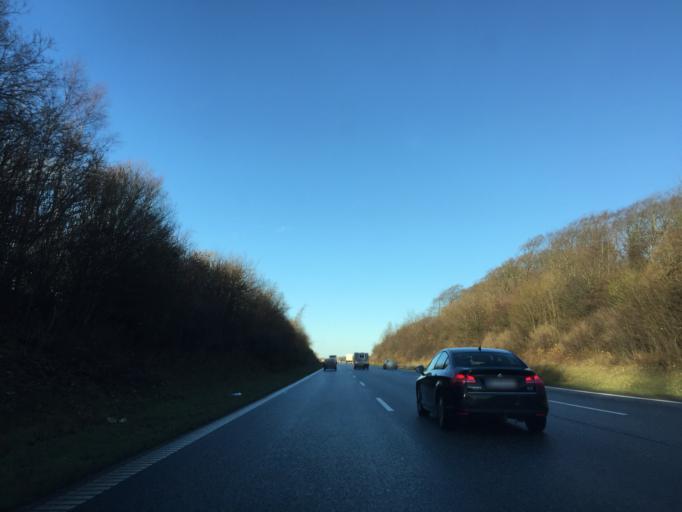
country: DK
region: South Denmark
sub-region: Fredericia Kommune
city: Taulov
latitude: 55.6056
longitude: 9.5855
